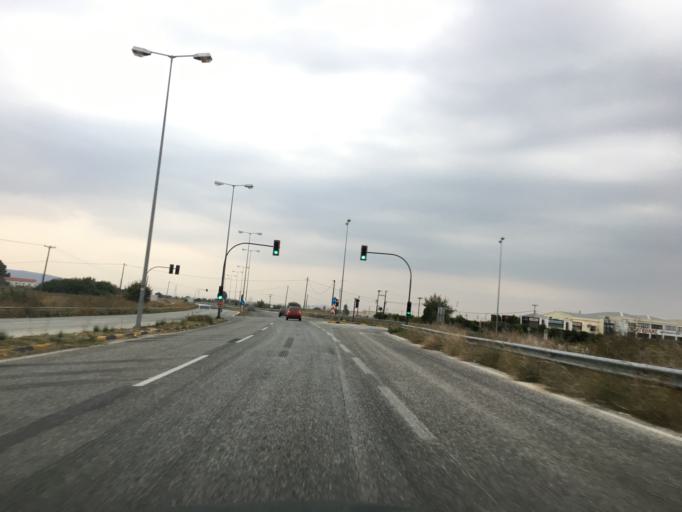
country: GR
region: Thessaly
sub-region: Trikala
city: Megalochori
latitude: 39.5625
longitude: 21.8565
